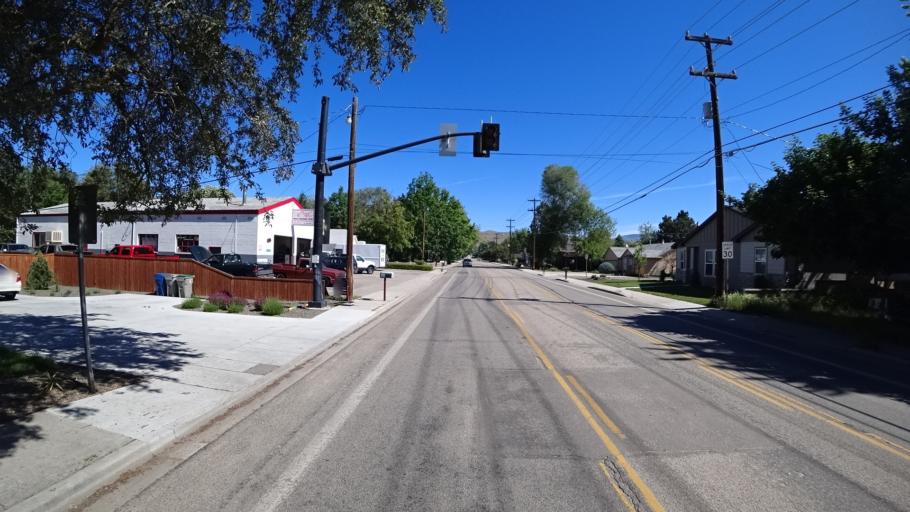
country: US
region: Idaho
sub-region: Ada County
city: Garden City
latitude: 43.6444
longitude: -116.2335
